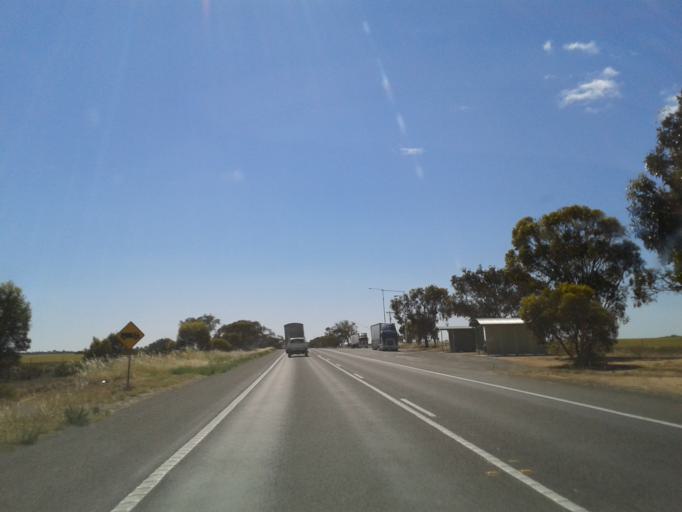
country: AU
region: New South Wales
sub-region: Wentworth
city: Dareton
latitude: -34.2311
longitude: 141.9888
